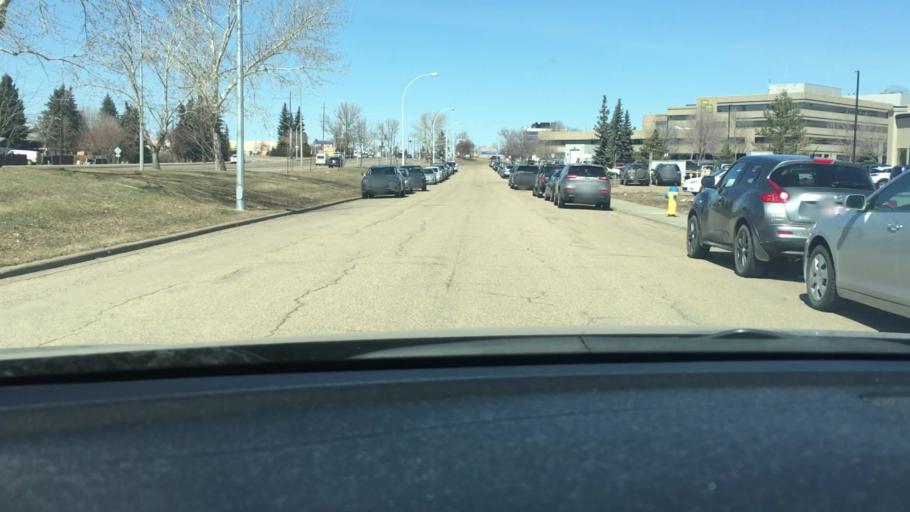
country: CA
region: Alberta
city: Edmonton
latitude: 53.5346
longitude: -113.4181
